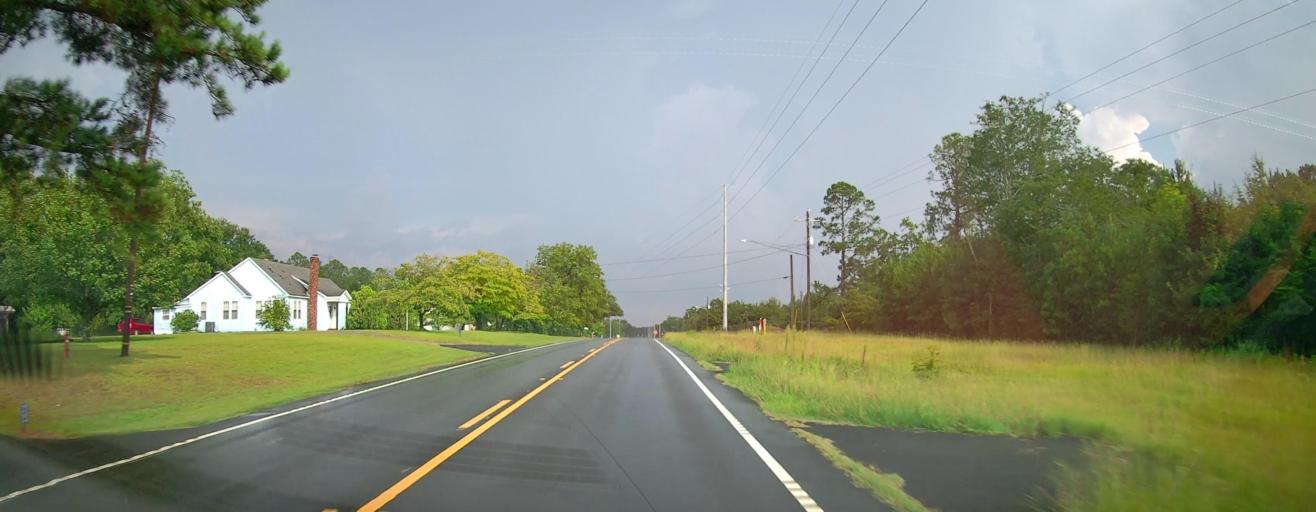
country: US
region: Georgia
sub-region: Twiggs County
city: Jeffersonville
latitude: 32.5951
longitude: -83.2328
